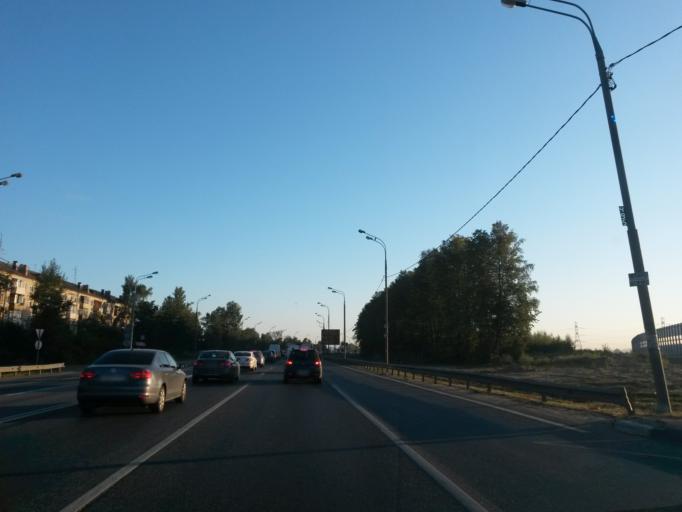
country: RU
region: Moskovskaya
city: Bolshevo
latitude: 55.9479
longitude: 37.8149
